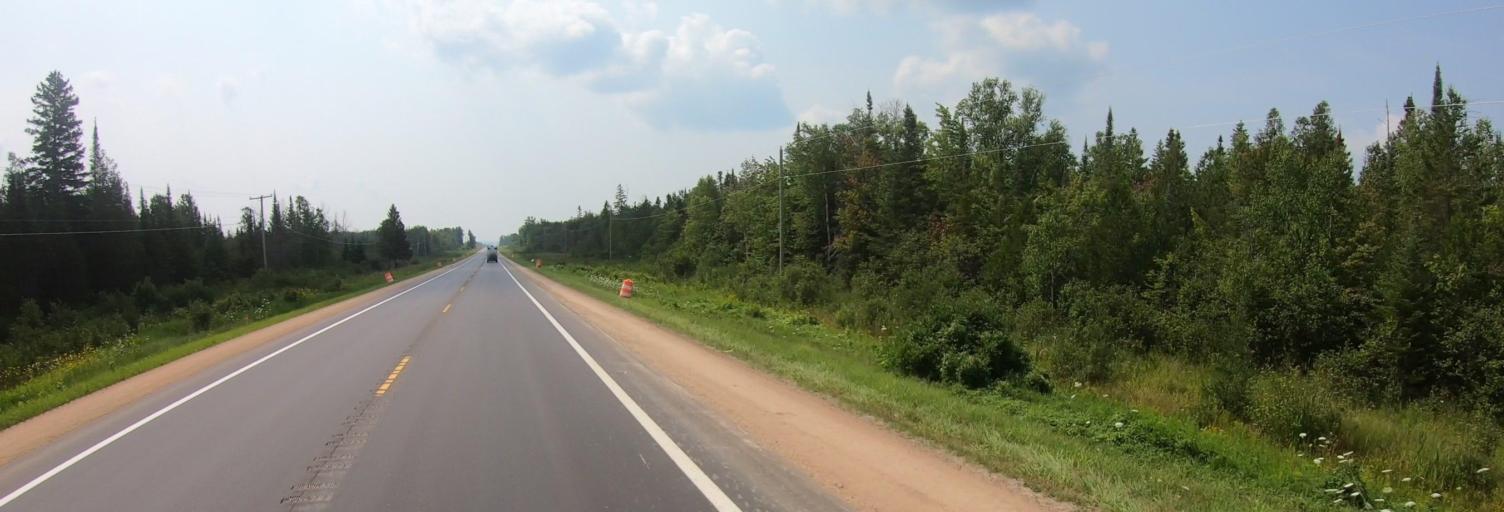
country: US
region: Michigan
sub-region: Luce County
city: Newberry
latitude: 46.4106
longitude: -85.5101
